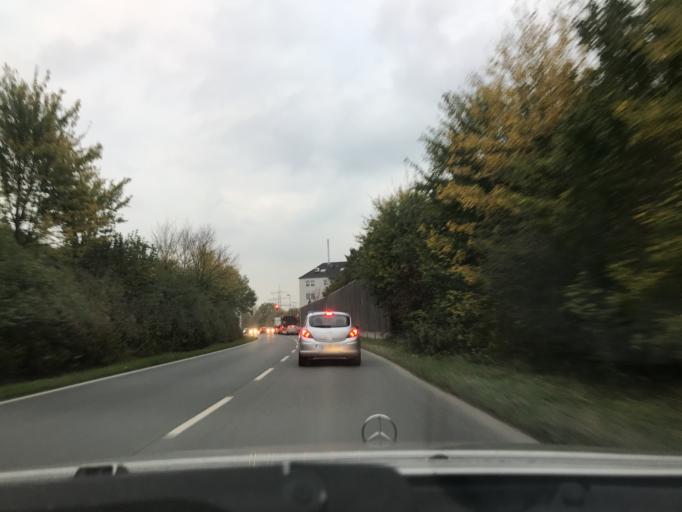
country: DE
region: North Rhine-Westphalia
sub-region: Regierungsbezirk Munster
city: Gelsenkirchen
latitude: 51.5302
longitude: 7.1293
